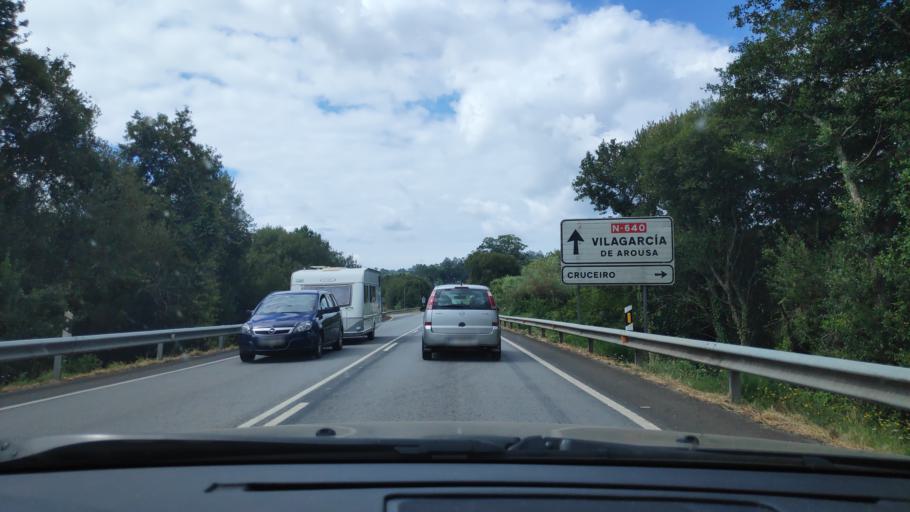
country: ES
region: Galicia
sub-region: Provincia de Pontevedra
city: Portas
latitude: 42.5867
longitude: -8.6926
